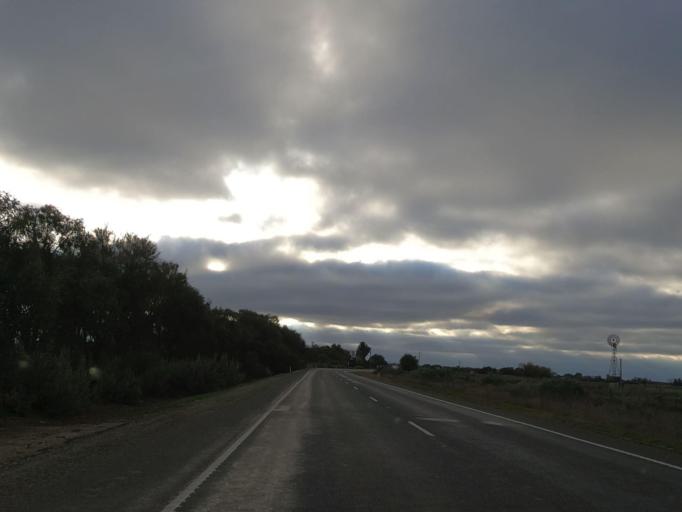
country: AU
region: Victoria
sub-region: Swan Hill
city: Swan Hill
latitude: -35.7227
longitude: 143.8885
